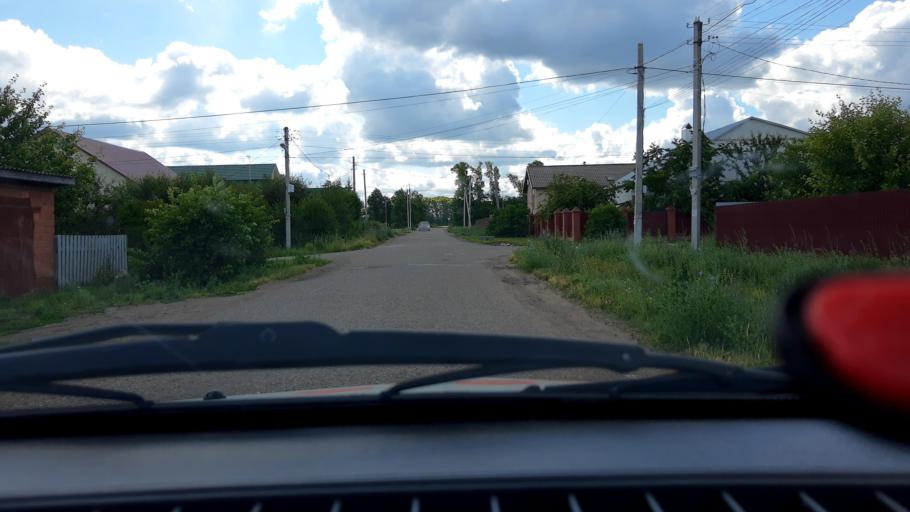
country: RU
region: Bashkortostan
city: Avdon
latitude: 54.4922
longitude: 55.8982
